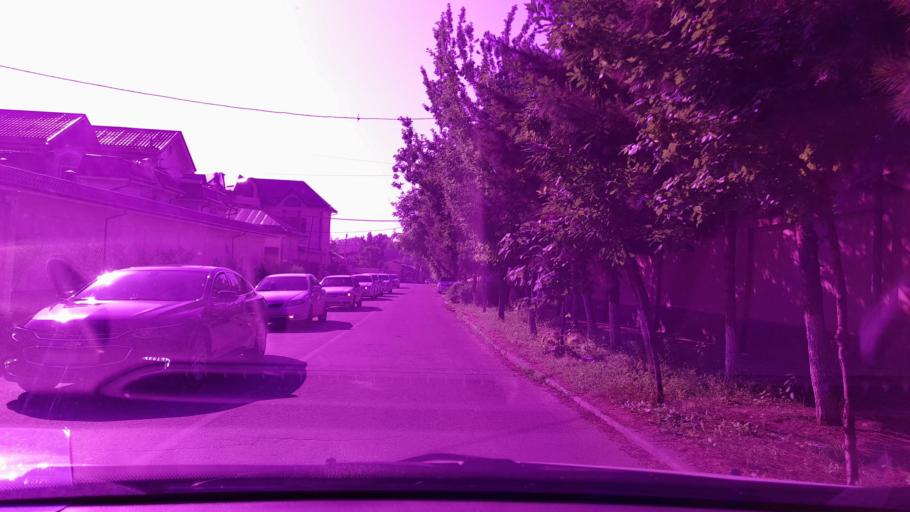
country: UZ
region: Toshkent
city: Salor
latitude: 41.3346
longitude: 69.3600
